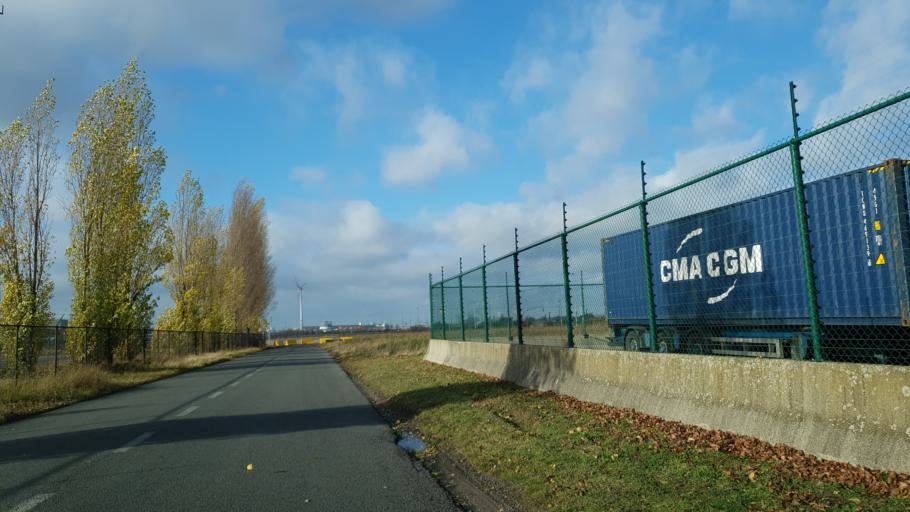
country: BE
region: Flanders
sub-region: Provincie Antwerpen
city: Stabroek
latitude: 51.2891
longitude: 4.3760
